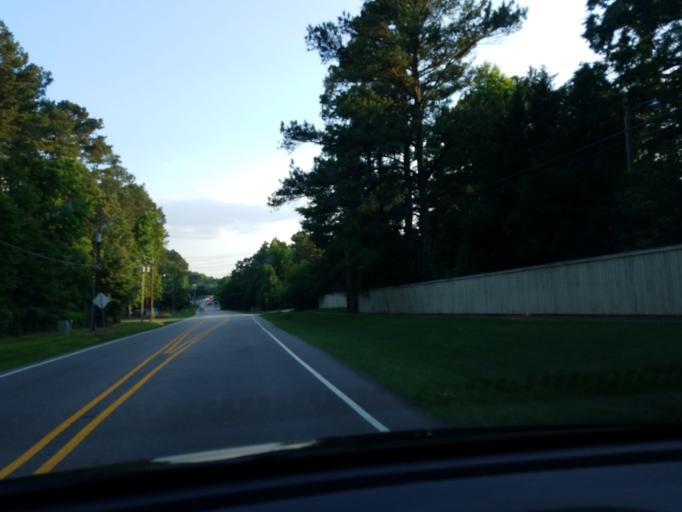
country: US
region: North Carolina
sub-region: Durham County
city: Durham
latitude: 35.9256
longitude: -78.9549
